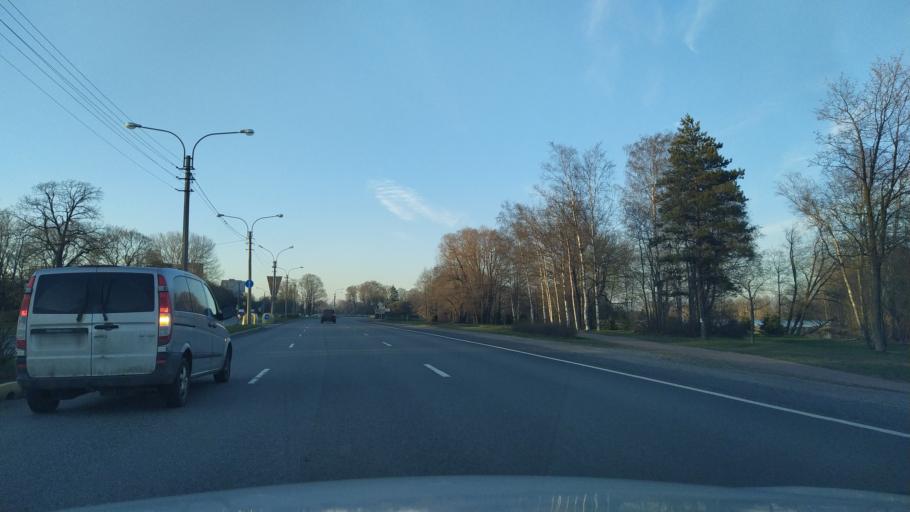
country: RU
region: St.-Petersburg
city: Razliv
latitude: 60.0912
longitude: 29.9744
